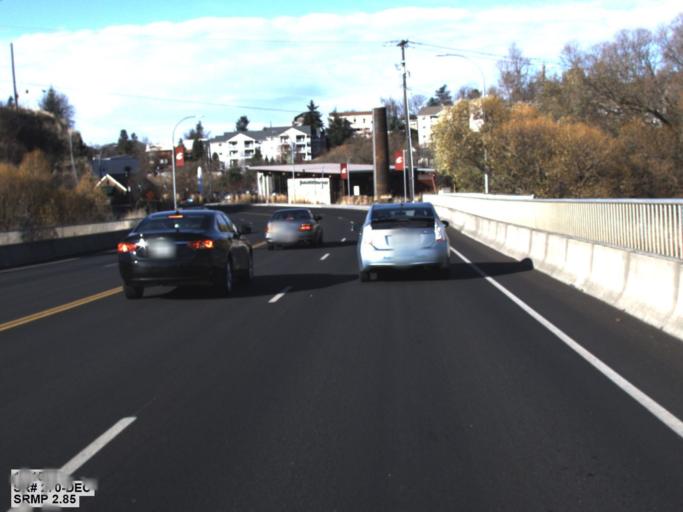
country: US
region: Washington
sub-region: Whitman County
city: Pullman
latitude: 46.7292
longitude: -117.1732
